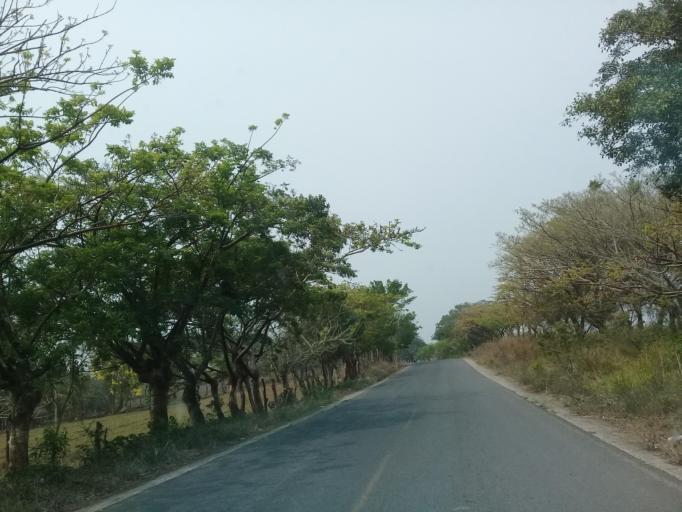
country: MX
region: Veracruz
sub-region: Medellin
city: La Laguna y Monte del Castillo
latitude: 18.9573
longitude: -96.1230
